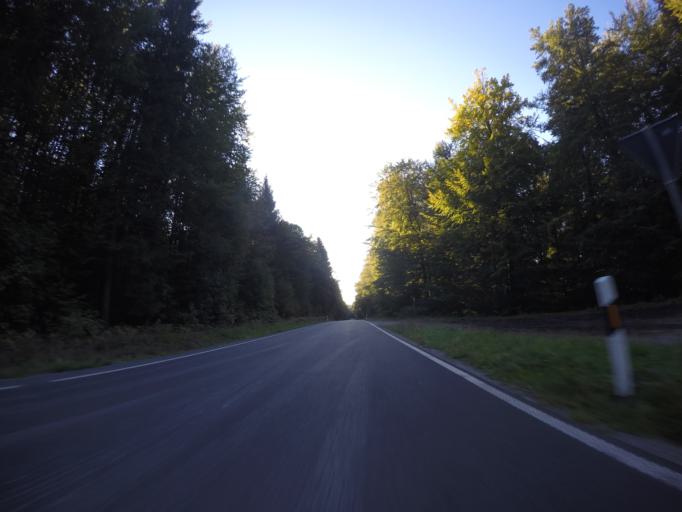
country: DE
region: Bavaria
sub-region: Regierungsbezirk Unterfranken
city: Altenbuch
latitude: 49.8598
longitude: 9.4239
